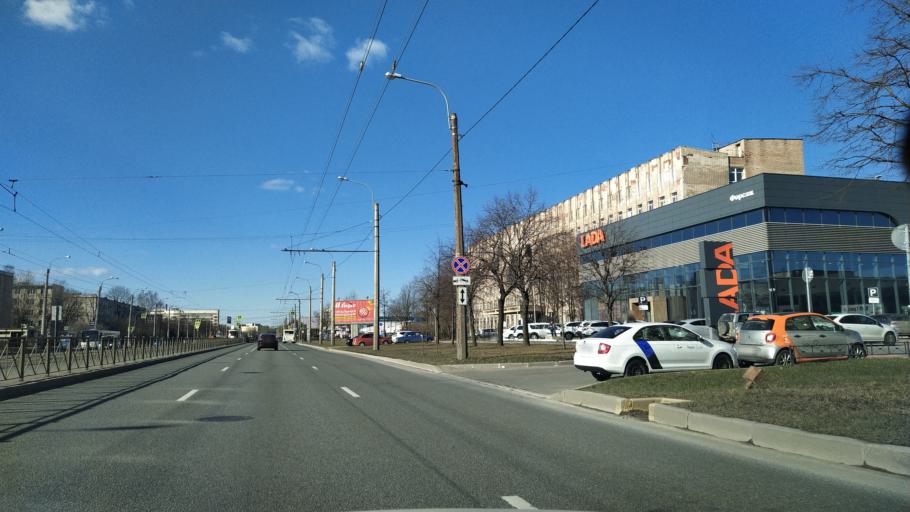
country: RU
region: St.-Petersburg
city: Kupchino
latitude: 59.8866
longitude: 30.3646
